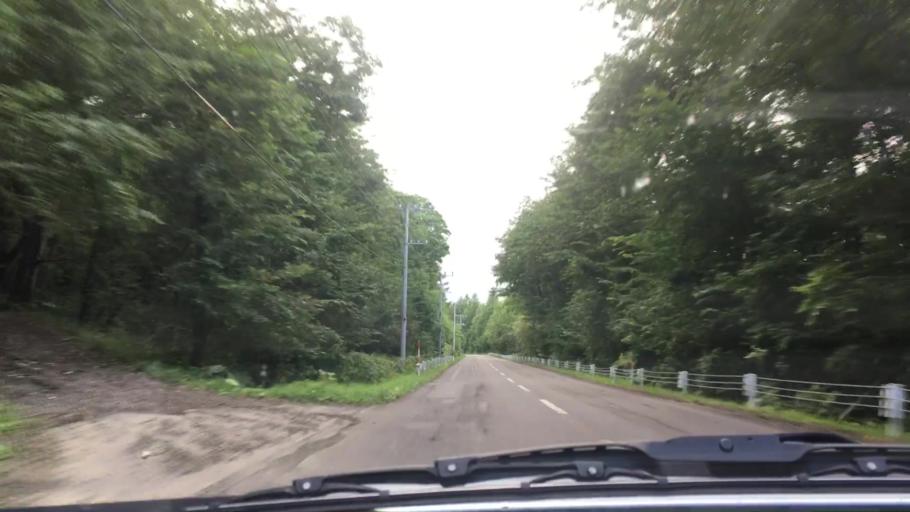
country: JP
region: Hokkaido
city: Otofuke
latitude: 43.1458
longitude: 142.8748
